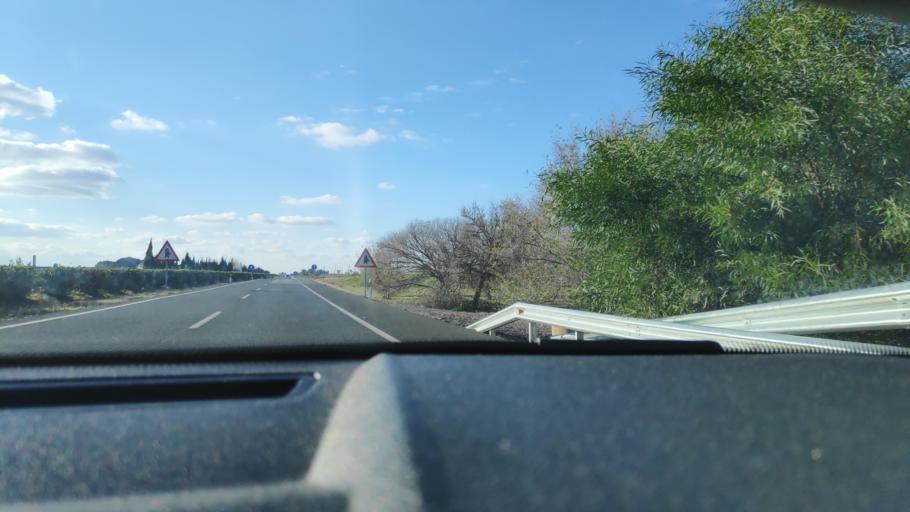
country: ES
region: Andalusia
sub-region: Provincia de Sevilla
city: La Luisiana
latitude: 37.5230
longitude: -5.1949
